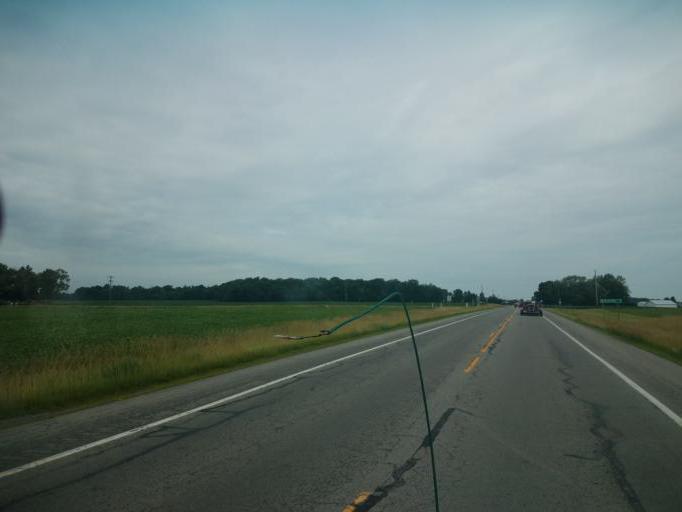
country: US
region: Ohio
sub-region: Hardin County
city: Ada
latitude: 40.7258
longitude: -83.7831
